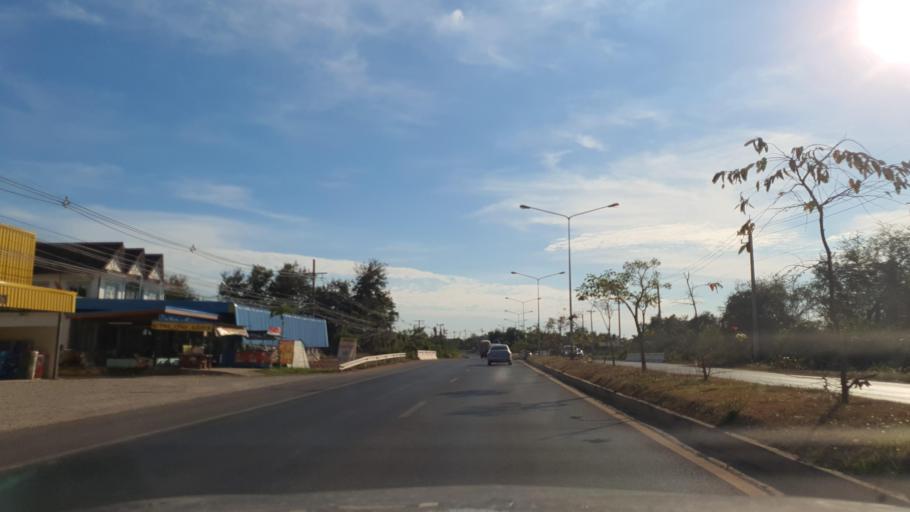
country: TH
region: Kalasin
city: Yang Talat
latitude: 16.3752
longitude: 103.3463
